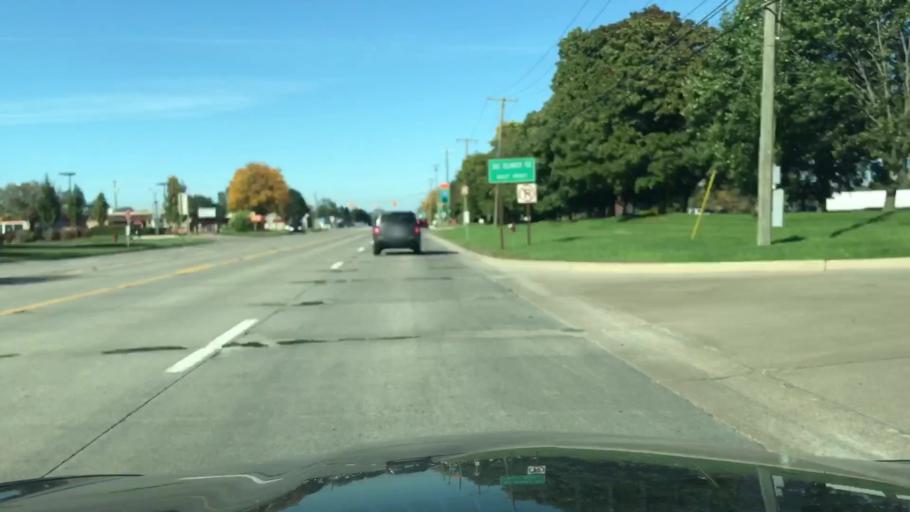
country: US
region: Michigan
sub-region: Macomb County
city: Sterling Heights
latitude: 42.5616
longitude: -83.0886
